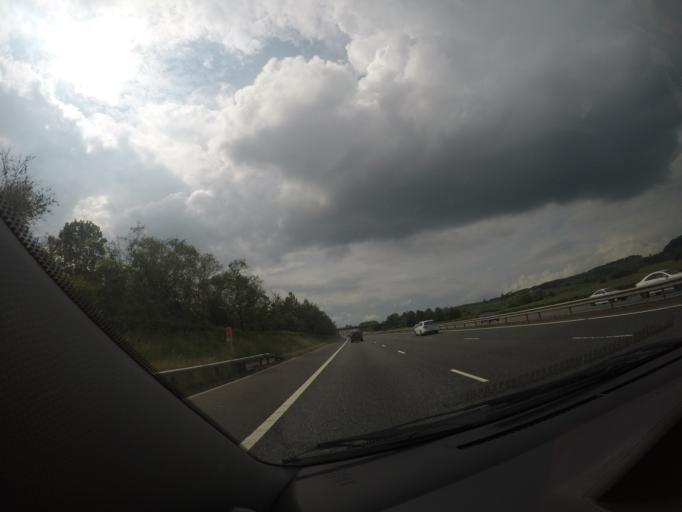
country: GB
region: Scotland
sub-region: Dumfries and Galloway
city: Lockerbie
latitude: 55.0709
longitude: -3.2940
